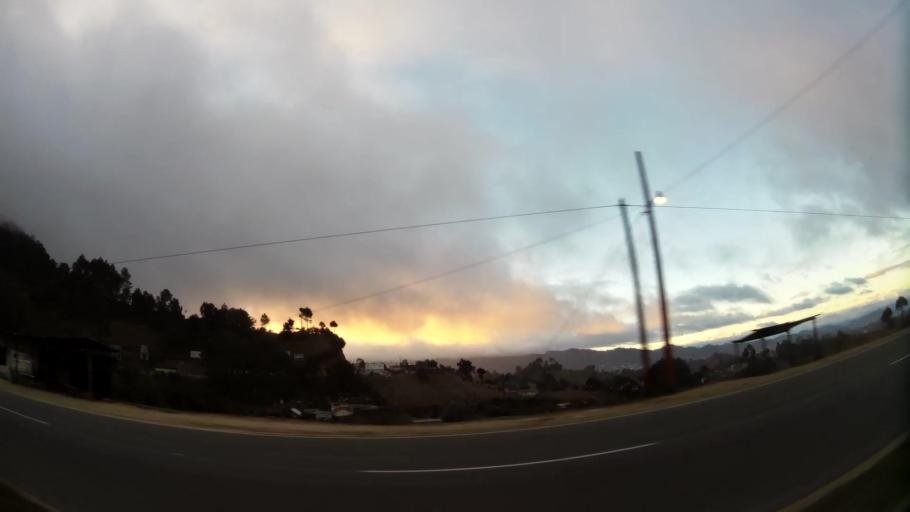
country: GT
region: Solola
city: Concepcion
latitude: 14.8492
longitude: -91.1328
